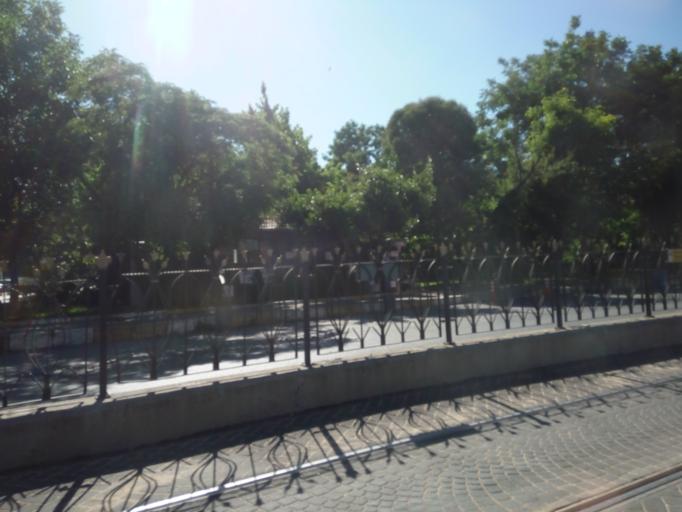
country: TR
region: Istanbul
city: Zeytinburnu
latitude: 41.0053
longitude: 28.9094
